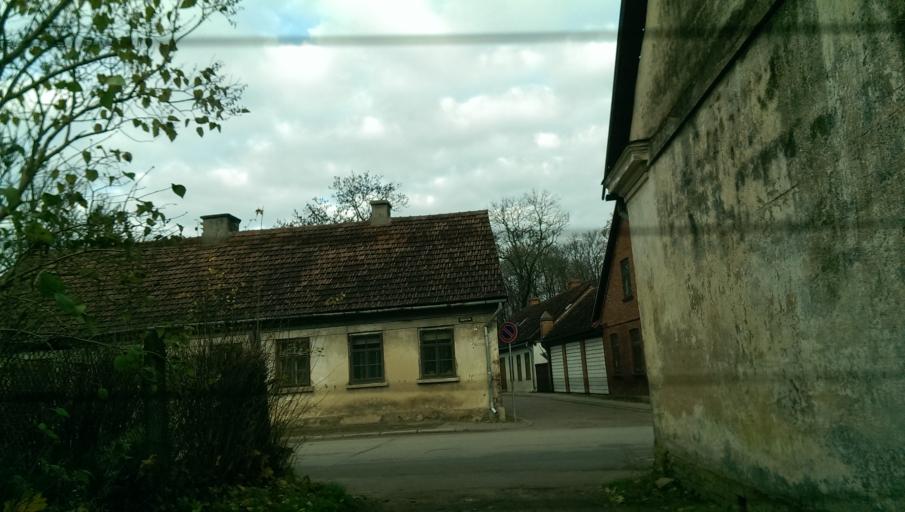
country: LV
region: Kuldigas Rajons
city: Kuldiga
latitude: 56.9646
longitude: 21.9747
